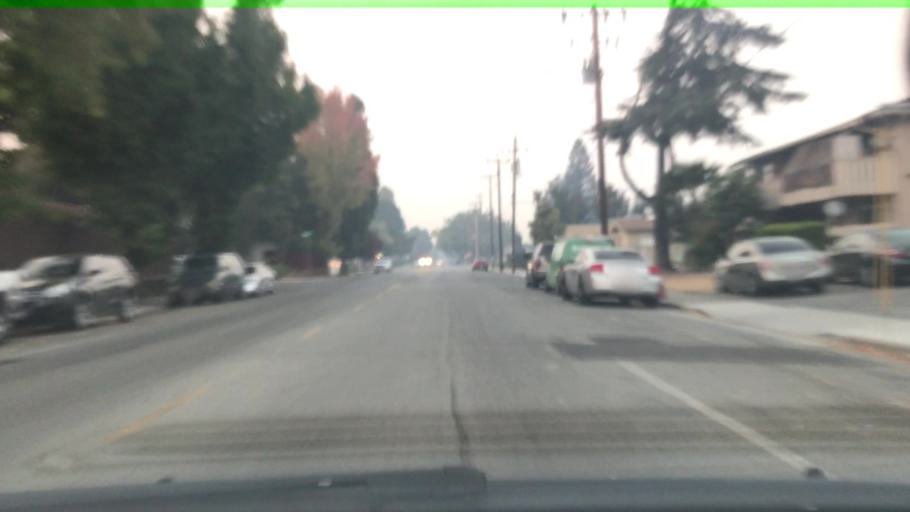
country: US
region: California
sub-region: Santa Clara County
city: Gilroy
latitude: 36.9987
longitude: -121.5746
